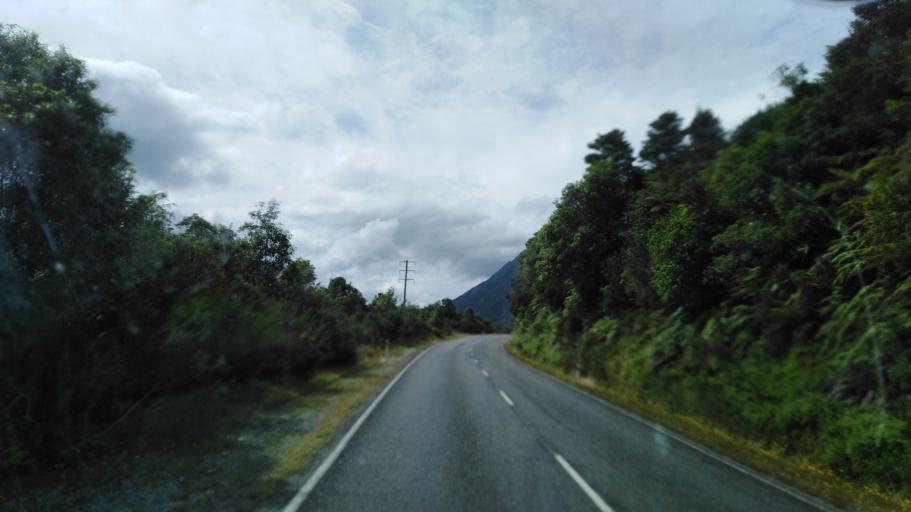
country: NZ
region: West Coast
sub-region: Grey District
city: Greymouth
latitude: -42.7366
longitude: 171.4551
